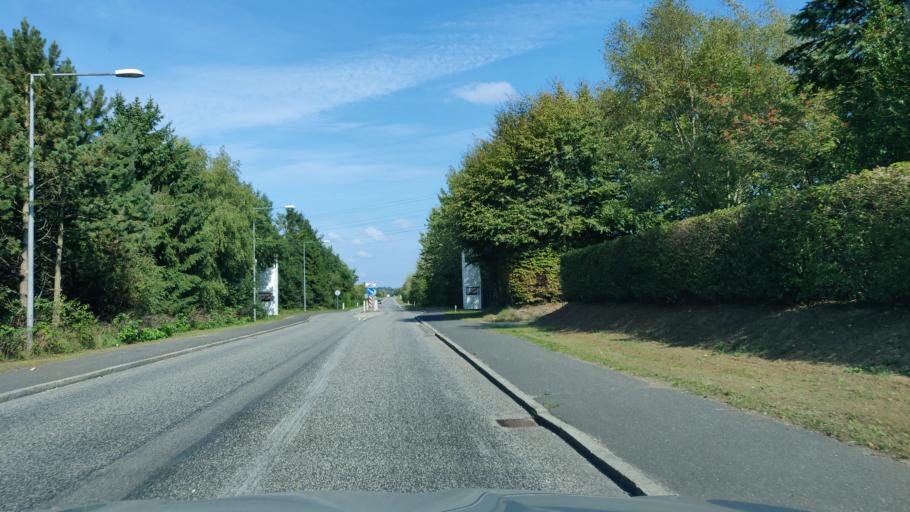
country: DK
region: Central Jutland
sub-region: Viborg Kommune
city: Stoholm
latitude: 56.3922
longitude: 8.9966
